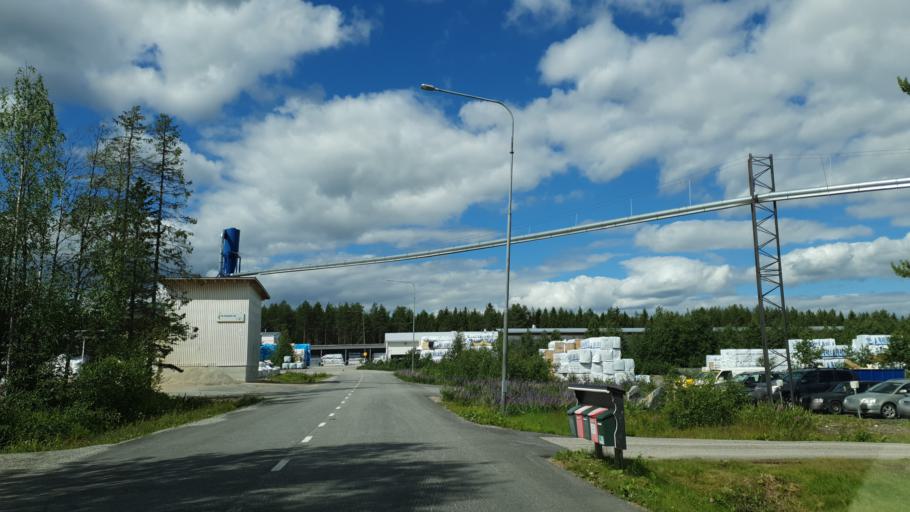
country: FI
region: Kainuu
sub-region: Kehys-Kainuu
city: Kuhmo
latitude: 64.1345
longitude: 29.4711
